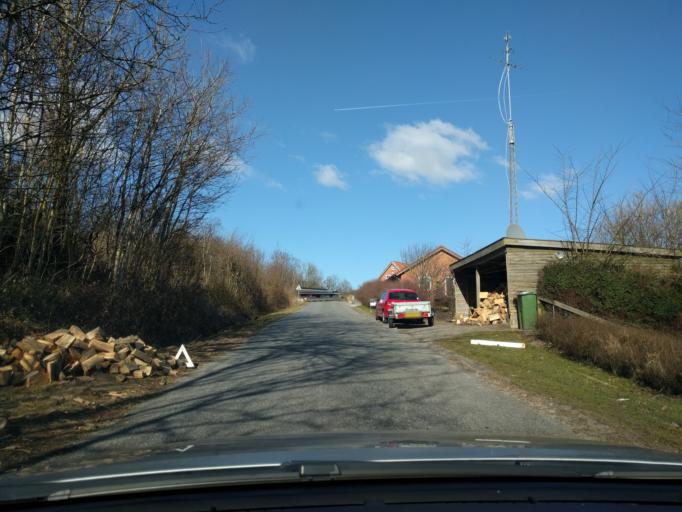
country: DK
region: South Denmark
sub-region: Aabenraa Kommune
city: Lojt Kirkeby
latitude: 55.1241
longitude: 9.4630
